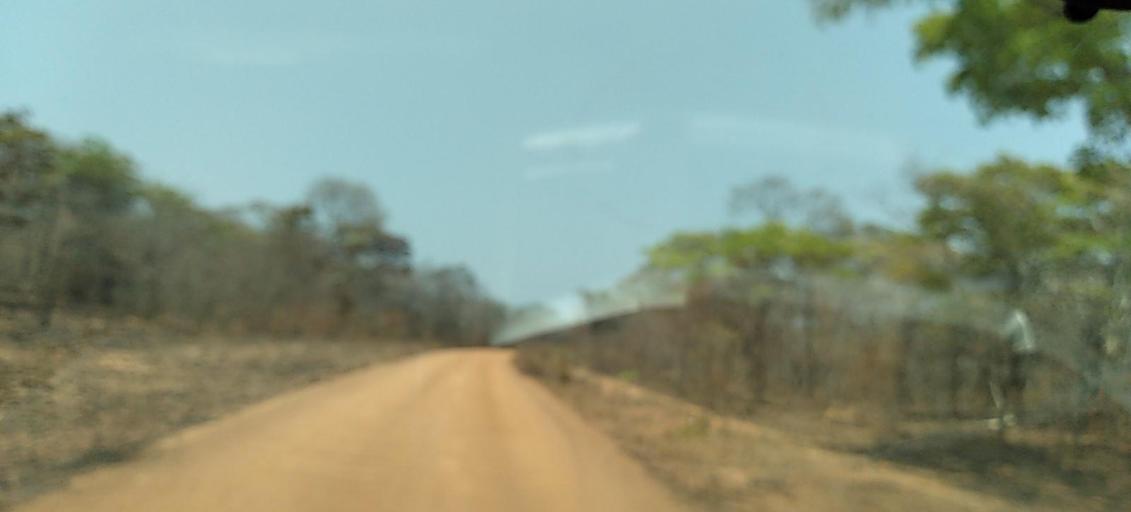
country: ZM
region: Central
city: Mumbwa
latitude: -14.3927
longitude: 26.4898
